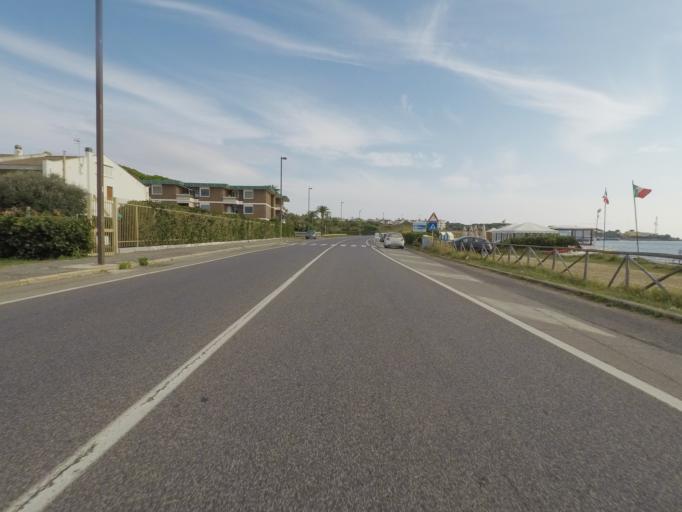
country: IT
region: Latium
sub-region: Citta metropolitana di Roma Capitale
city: Santa Marinella
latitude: 42.0389
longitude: 11.8312
